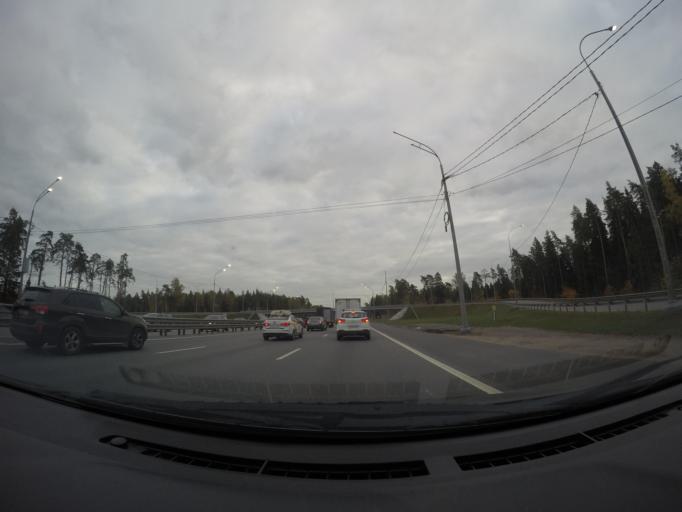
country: RU
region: Moskovskaya
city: Zarya
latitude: 55.8081
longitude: 38.0659
